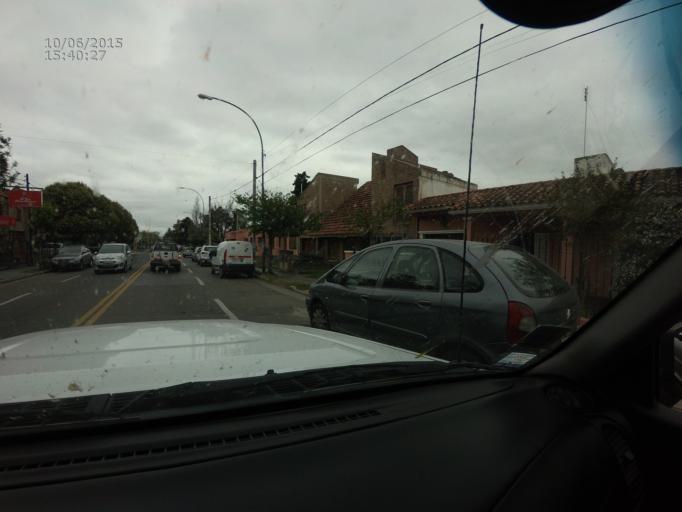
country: AR
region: Cordoba
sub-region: Departamento de Capital
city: Cordoba
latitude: -31.3642
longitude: -64.2263
